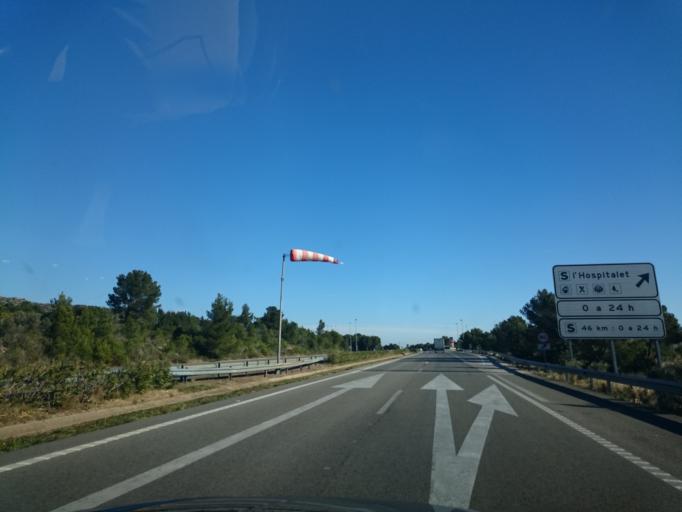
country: ES
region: Catalonia
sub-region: Provincia de Tarragona
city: Colldejou
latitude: 40.9832
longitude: 0.8913
